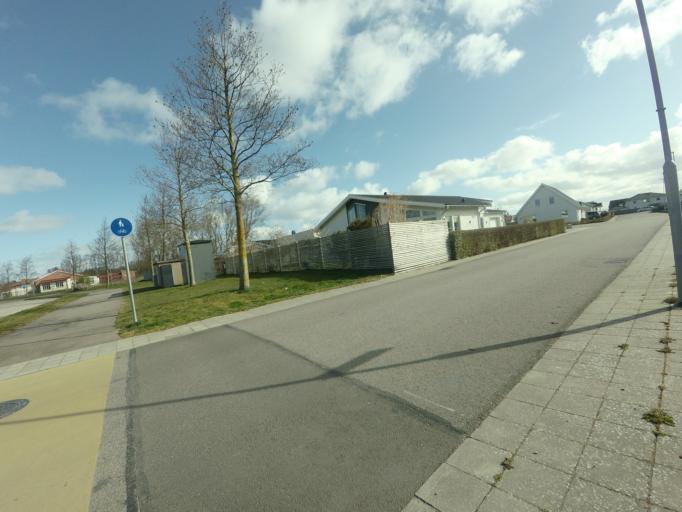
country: SE
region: Skane
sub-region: Hoganas Kommun
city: Hoganas
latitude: 56.1740
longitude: 12.5732
